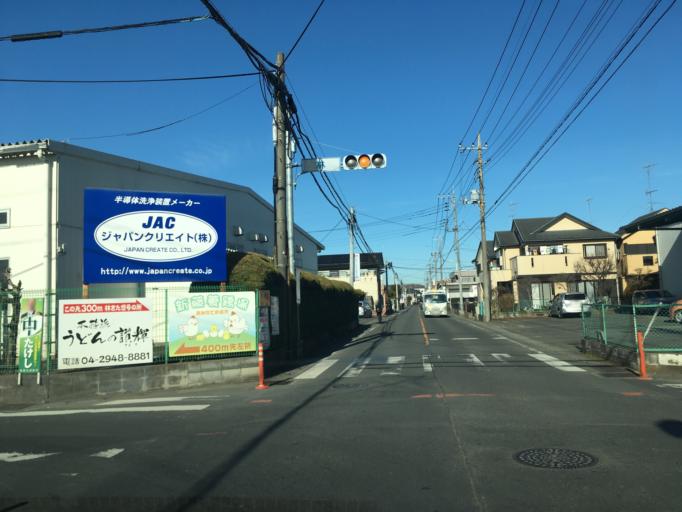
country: JP
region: Saitama
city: Sayama
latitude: 35.8019
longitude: 139.3957
